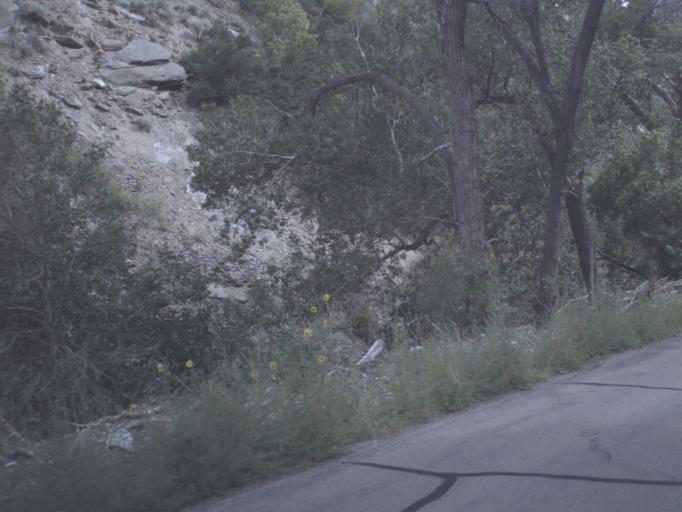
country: US
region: Utah
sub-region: Utah County
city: Cedar Hills
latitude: 40.4364
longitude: -111.7273
